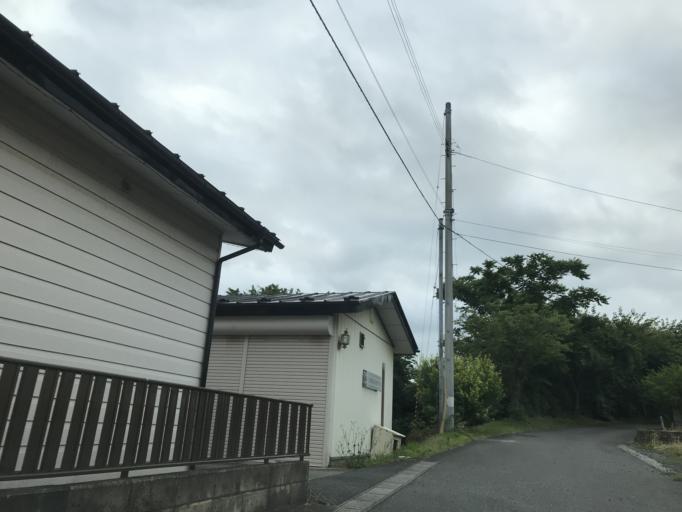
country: JP
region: Iwate
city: Ichinoseki
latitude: 38.9175
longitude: 141.1276
